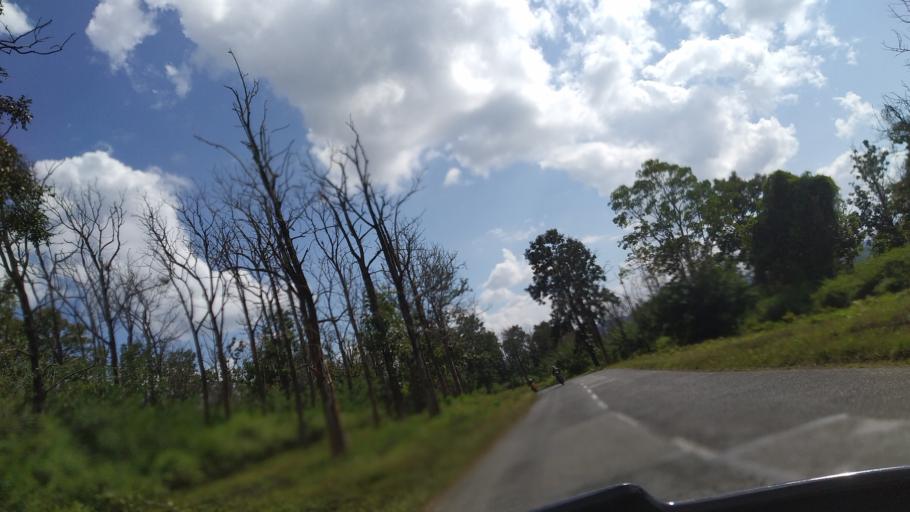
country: IN
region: Kerala
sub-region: Wayanad
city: Panamaram
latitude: 11.9259
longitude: 76.0659
